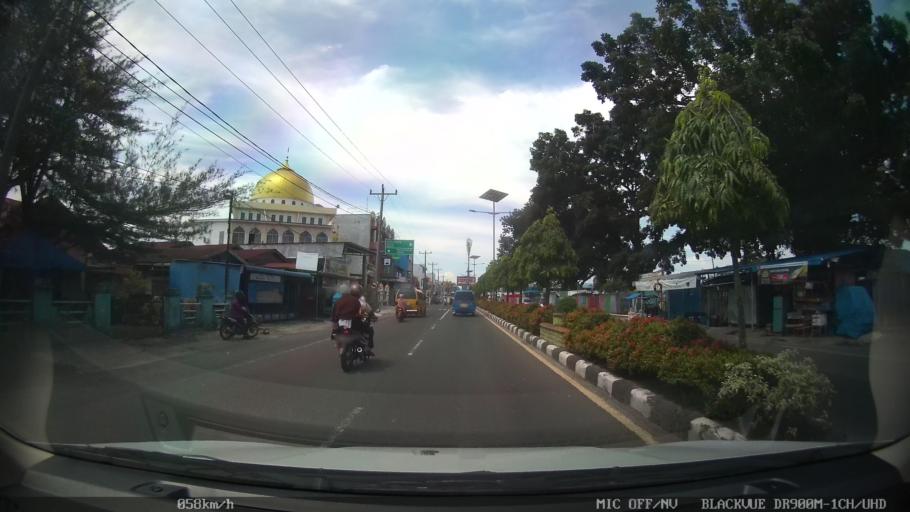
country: ID
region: North Sumatra
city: Binjai
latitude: 3.6197
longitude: 98.5010
